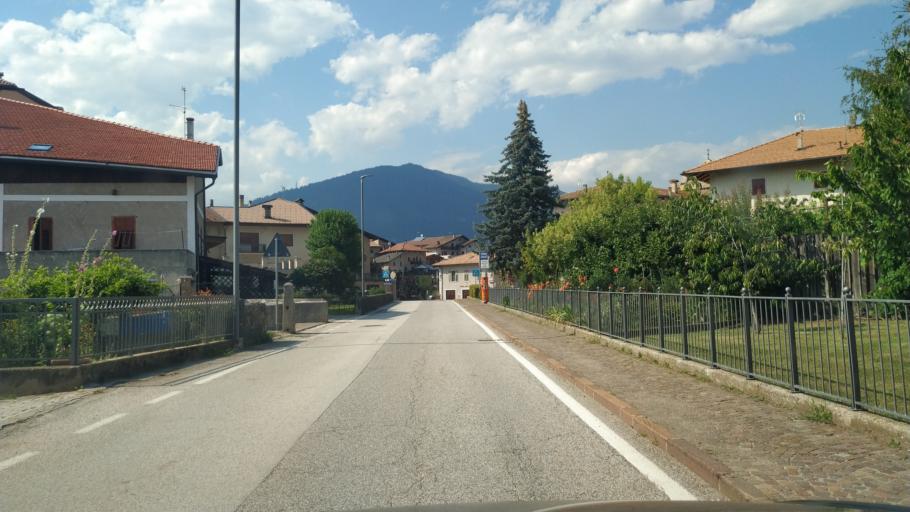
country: IT
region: Trentino-Alto Adige
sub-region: Provincia di Trento
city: Sanzeno
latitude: 46.3747
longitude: 11.0764
